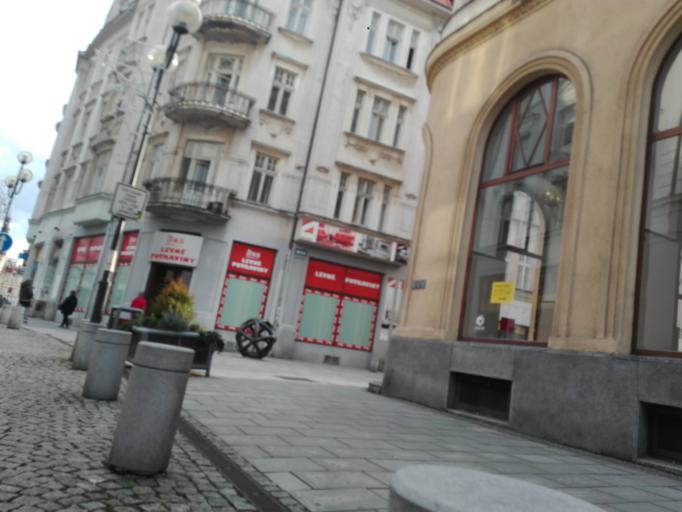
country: CZ
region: Moravskoslezsky
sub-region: Okres Ostrava-Mesto
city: Ostrava
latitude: 49.8366
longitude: 18.2902
